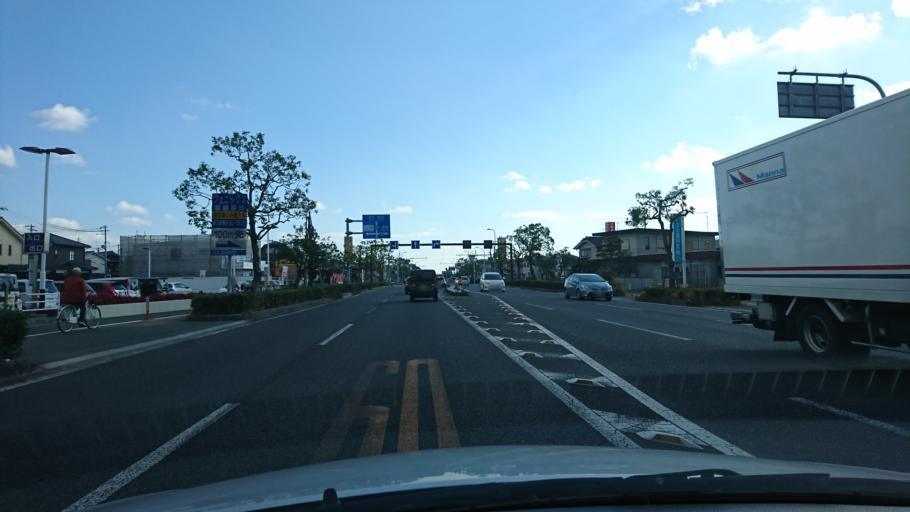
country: JP
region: Hyogo
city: Kakogawacho-honmachi
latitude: 34.7176
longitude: 134.8755
